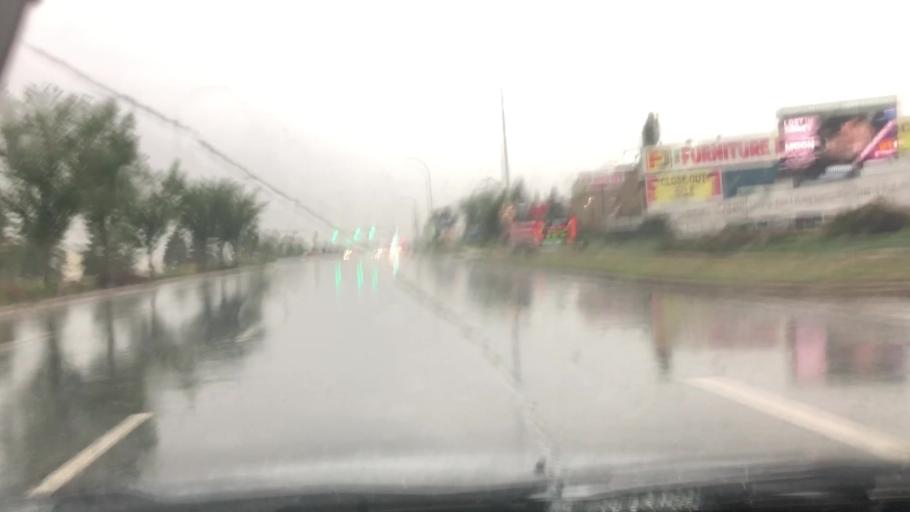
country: CA
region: Alberta
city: St. Albert
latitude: 53.5960
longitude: -113.5714
